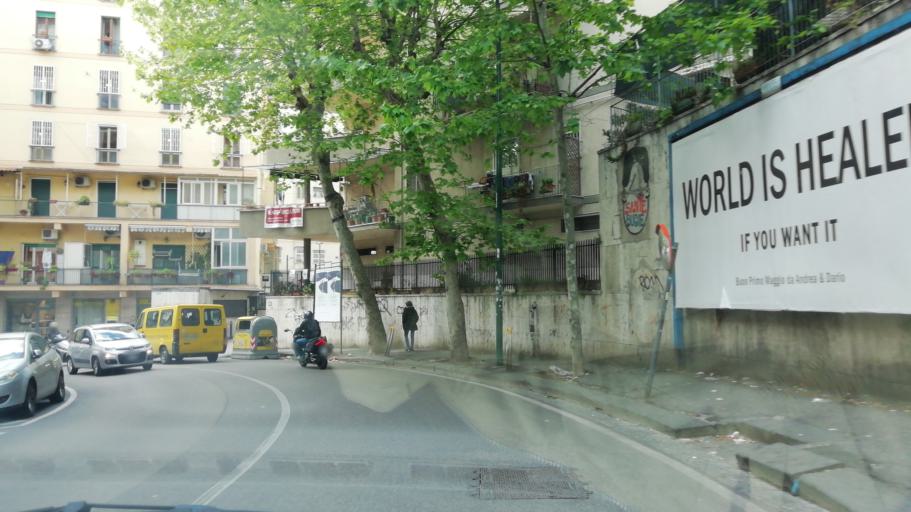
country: IT
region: Campania
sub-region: Provincia di Napoli
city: Napoli
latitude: 40.8564
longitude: 14.2291
